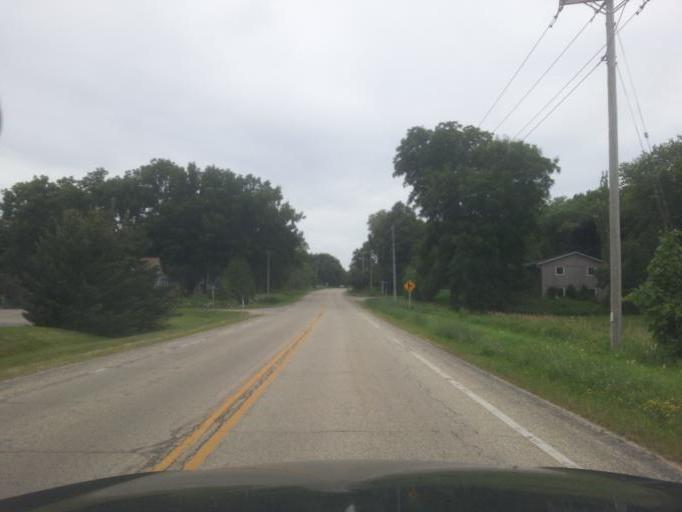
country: US
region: Wisconsin
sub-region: Dane County
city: Cottage Grove
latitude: 43.0748
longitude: -89.2659
